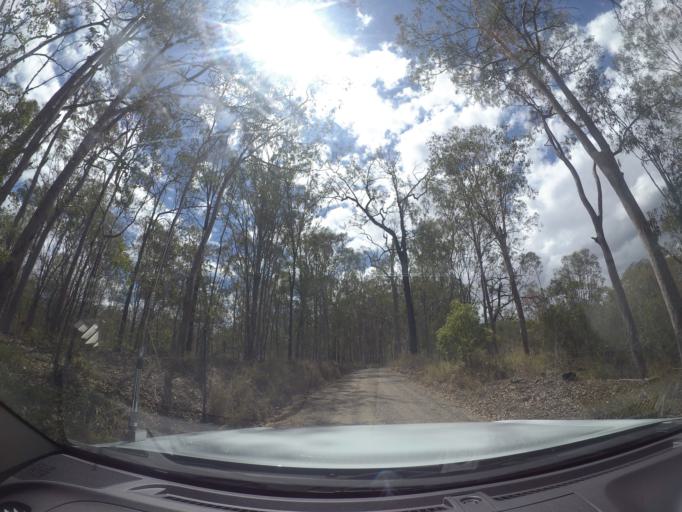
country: AU
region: Queensland
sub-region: Logan
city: Cedar Vale
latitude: -27.8975
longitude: 153.0440
